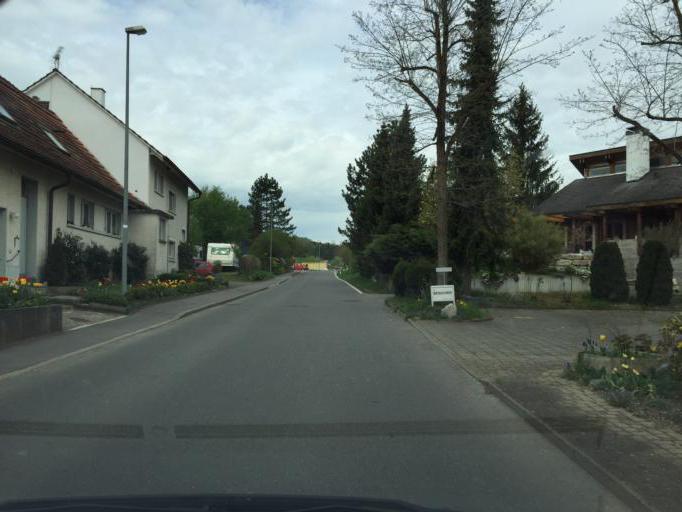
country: DE
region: Baden-Wuerttemberg
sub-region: Freiburg Region
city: Busingen
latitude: 47.6992
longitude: 8.6889
